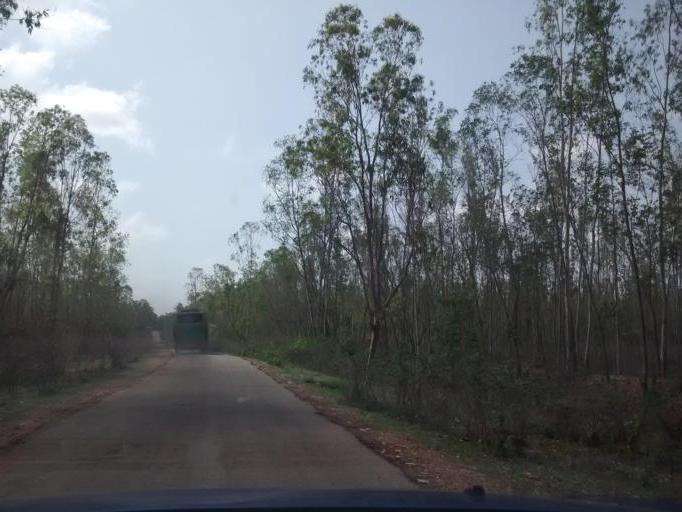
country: IN
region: Karnataka
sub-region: Hassan
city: Arkalgud
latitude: 12.7056
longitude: 76.1506
